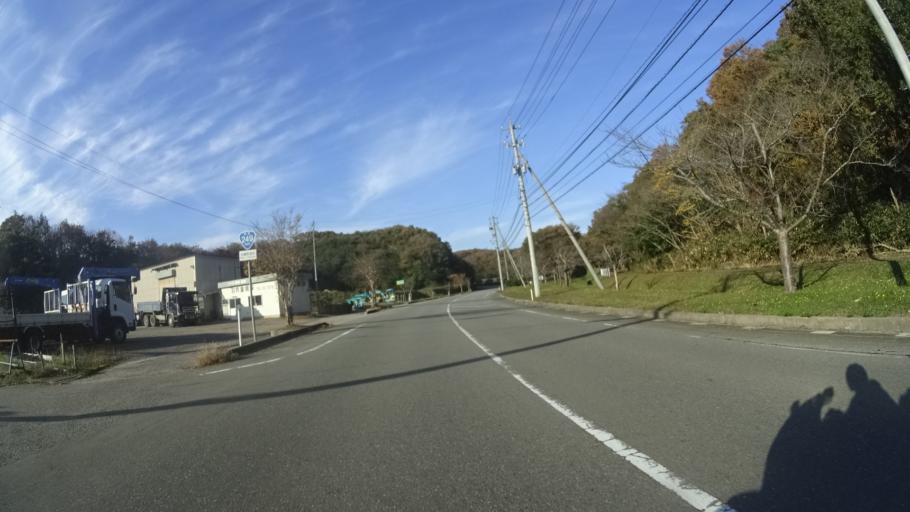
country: JP
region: Ishikawa
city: Hakui
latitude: 37.0289
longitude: 136.7805
